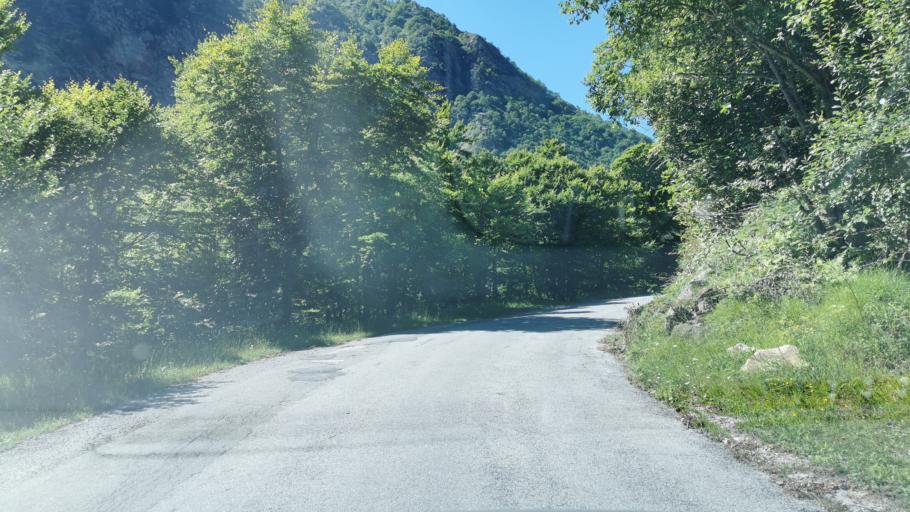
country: IT
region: Piedmont
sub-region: Provincia di Cuneo
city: Entracque
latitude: 44.1911
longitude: 7.3547
